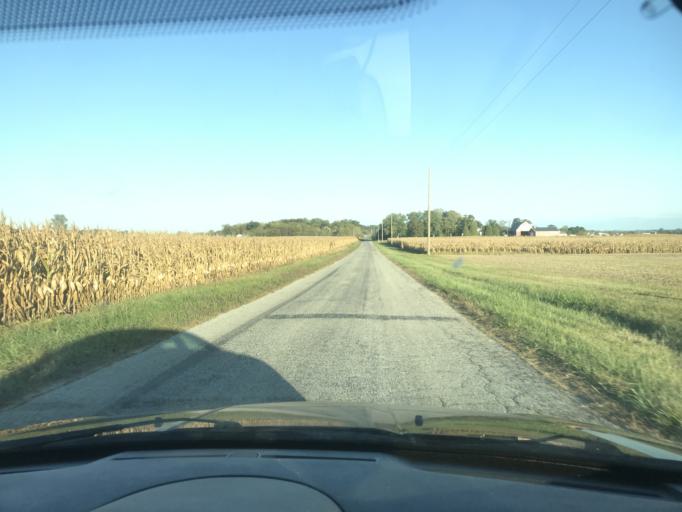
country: US
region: Ohio
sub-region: Logan County
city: West Liberty
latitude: 40.2317
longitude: -83.8055
